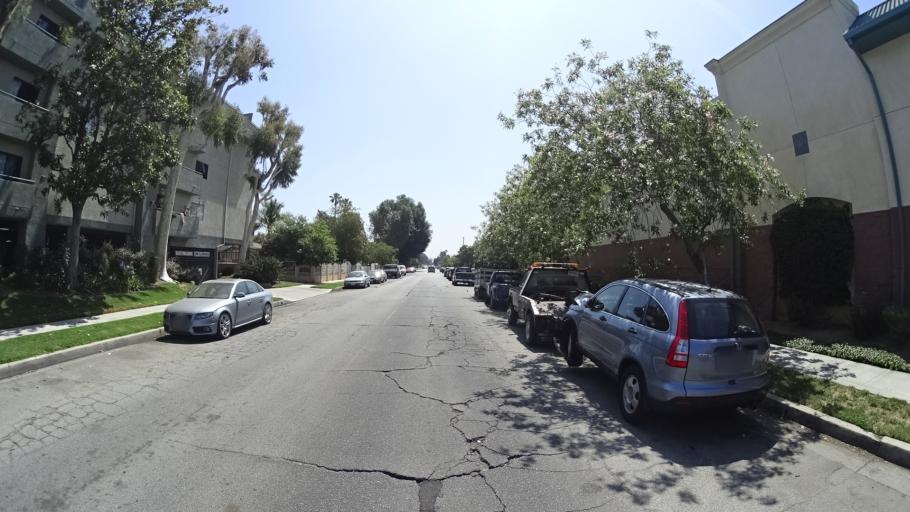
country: US
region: California
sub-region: Los Angeles County
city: Van Nuys
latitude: 34.2048
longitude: -118.4659
